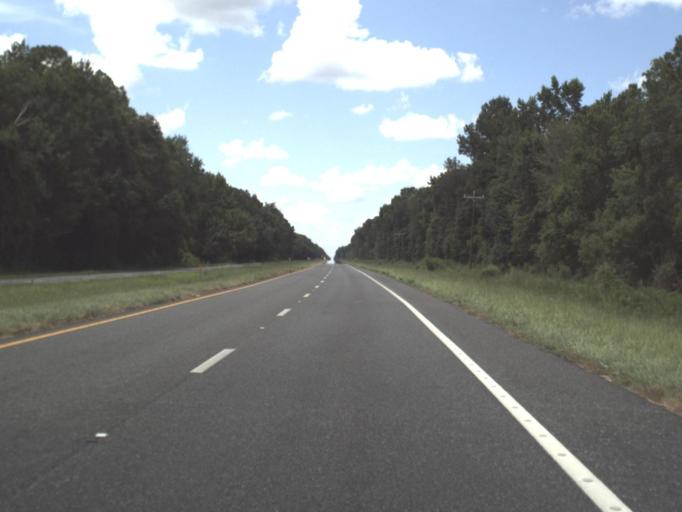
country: US
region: Florida
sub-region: Taylor County
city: Perry
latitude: 30.1889
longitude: -83.6445
